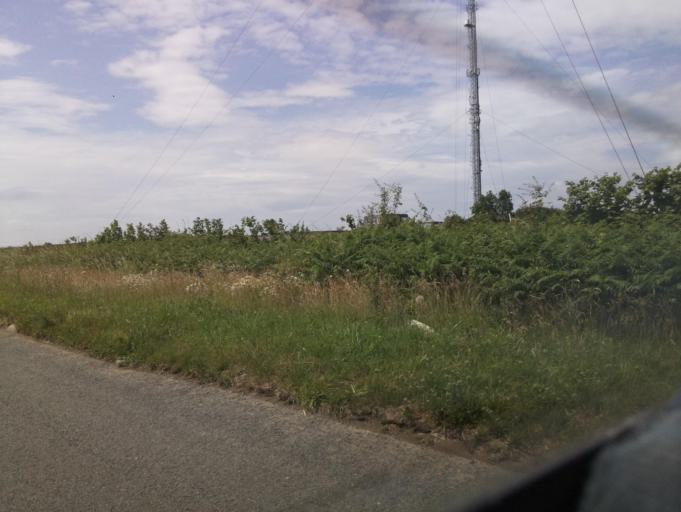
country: GB
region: Wales
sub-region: Vale of Glamorgan
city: Cowbridge
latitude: 51.4560
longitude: -3.4014
